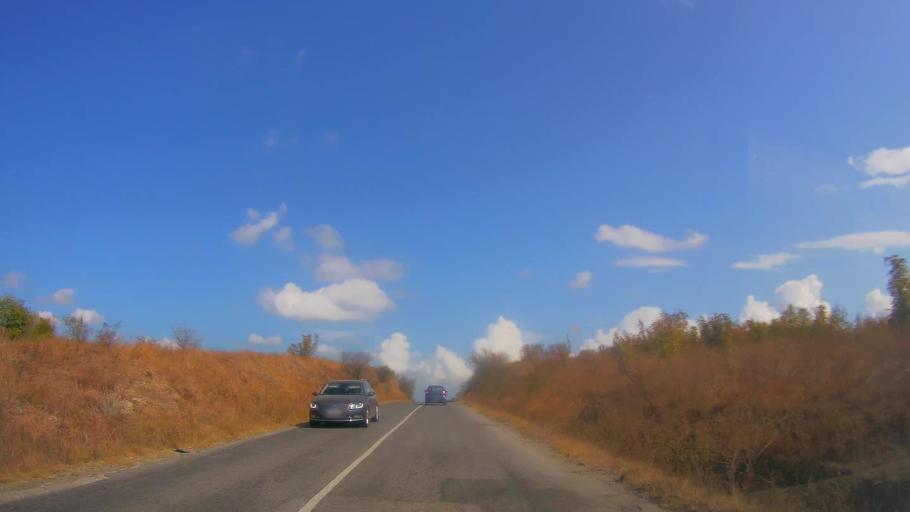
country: BG
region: Burgas
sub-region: Obshtina Burgas
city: Burgas
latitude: 42.4769
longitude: 27.3922
